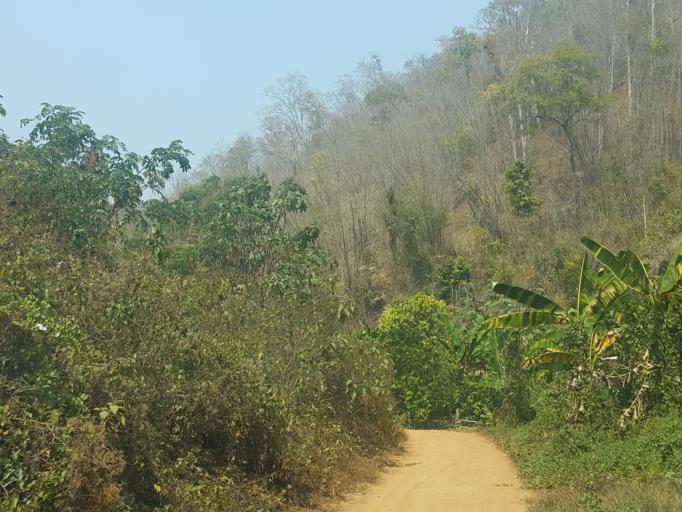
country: TH
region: Chiang Mai
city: Hang Dong
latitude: 18.7563
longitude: 98.8246
